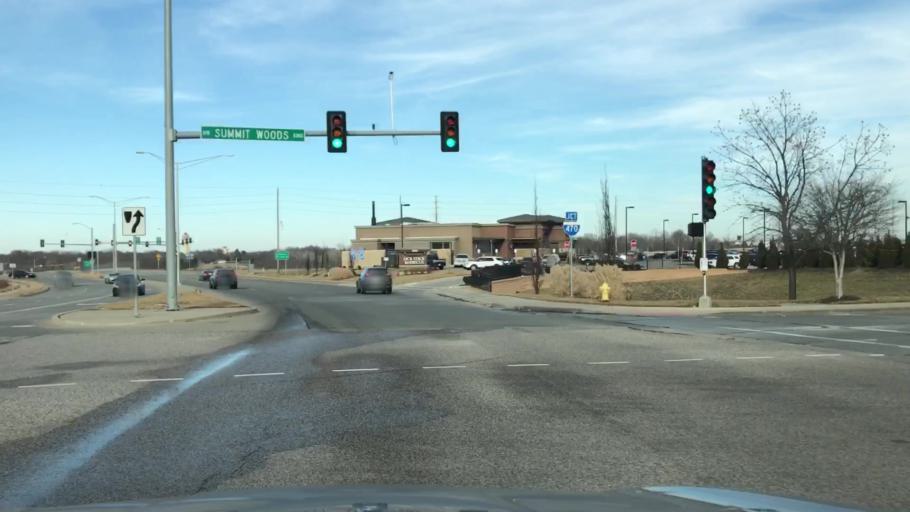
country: US
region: Missouri
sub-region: Jackson County
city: Lees Summit
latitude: 38.9312
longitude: -94.4124
